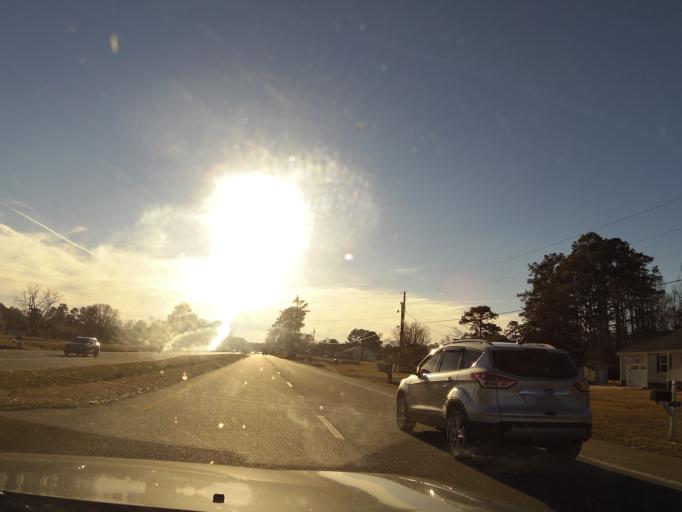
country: US
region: Virginia
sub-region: City of Franklin
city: Franklin
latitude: 36.6644
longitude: -76.8053
